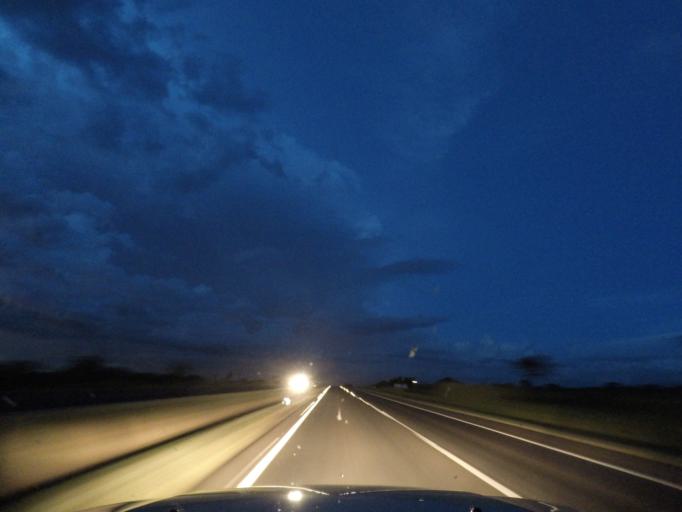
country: BR
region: Minas Gerais
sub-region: Uberlandia
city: Uberlandia
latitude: -19.2152
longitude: -48.1472
